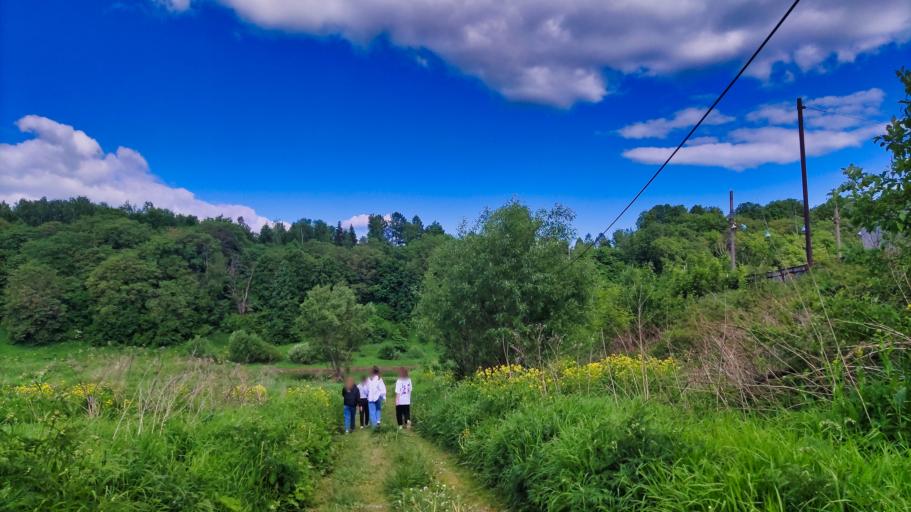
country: RU
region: Tverskaya
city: Rzhev
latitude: 56.2478
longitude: 34.3486
